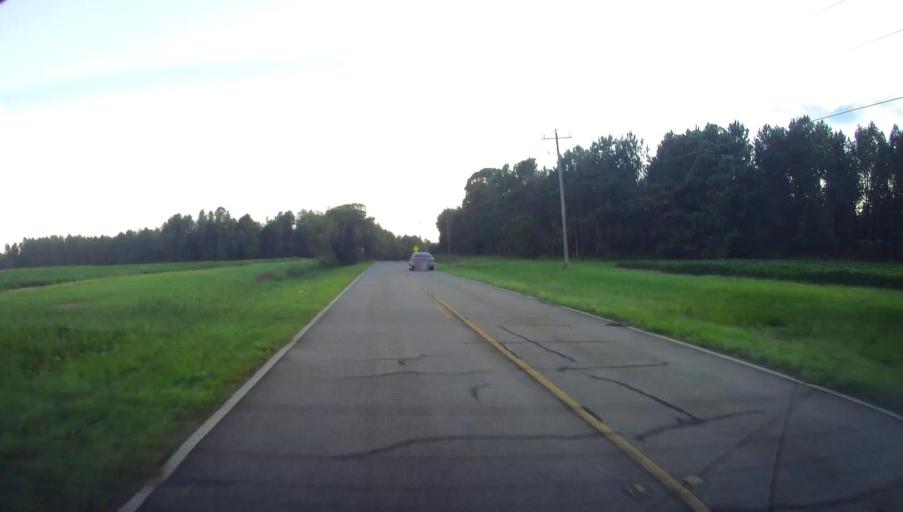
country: US
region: Georgia
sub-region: Peach County
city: Fort Valley
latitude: 32.6007
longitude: -83.8360
